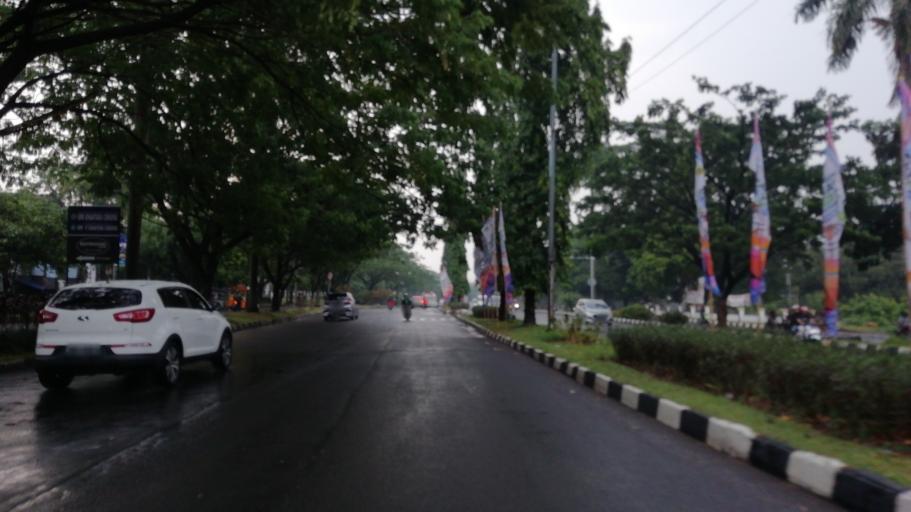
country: ID
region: West Java
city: Cibinong
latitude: -6.4845
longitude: 106.8352
